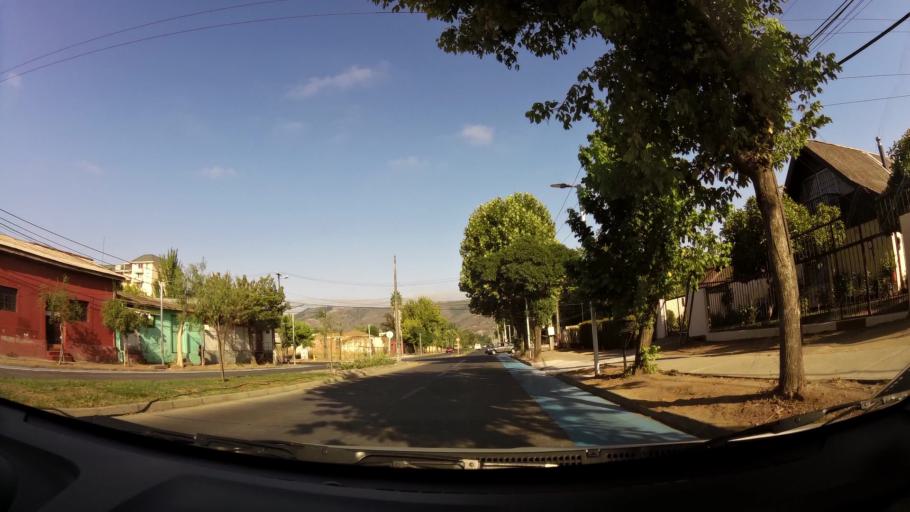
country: CL
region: Maule
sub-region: Provincia de Talca
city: Talca
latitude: -35.4113
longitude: -71.6591
